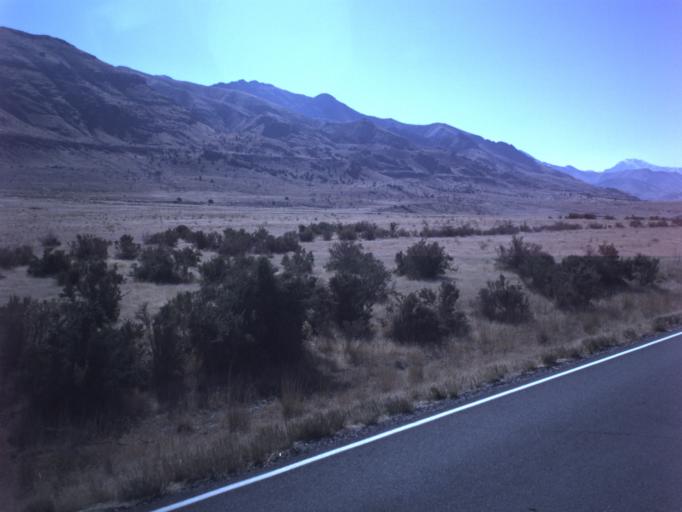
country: US
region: Utah
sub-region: Tooele County
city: Grantsville
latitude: 40.7005
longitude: -112.6658
